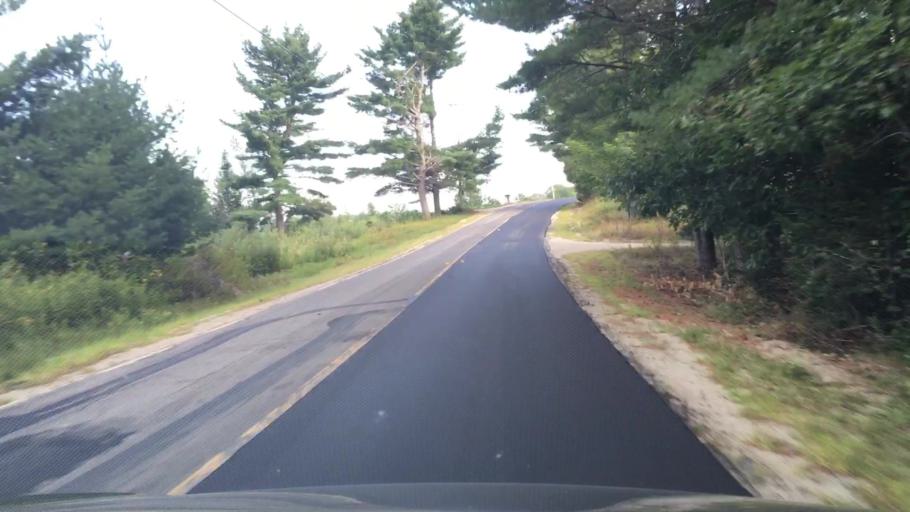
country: US
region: Maine
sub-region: Hancock County
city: Surry
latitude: 44.5162
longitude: -68.6045
